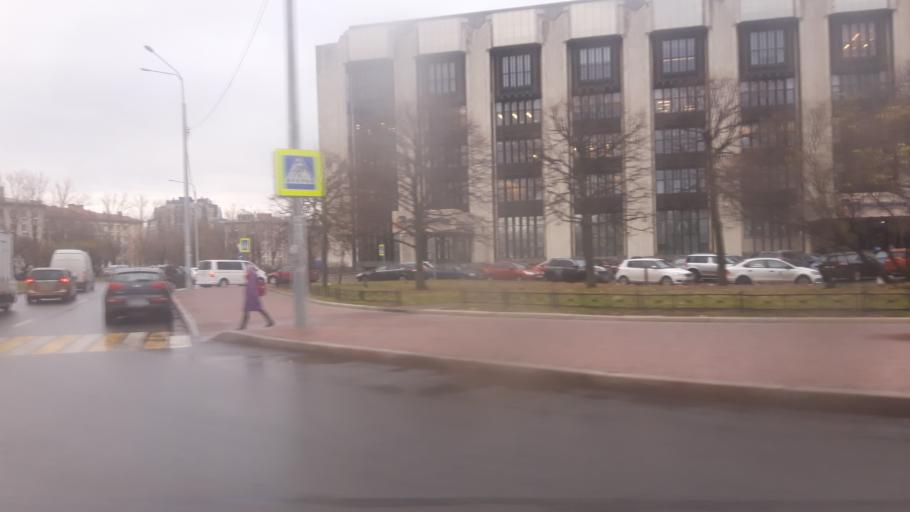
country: RU
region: St.-Petersburg
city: Kupchino
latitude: 59.8435
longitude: 30.3236
